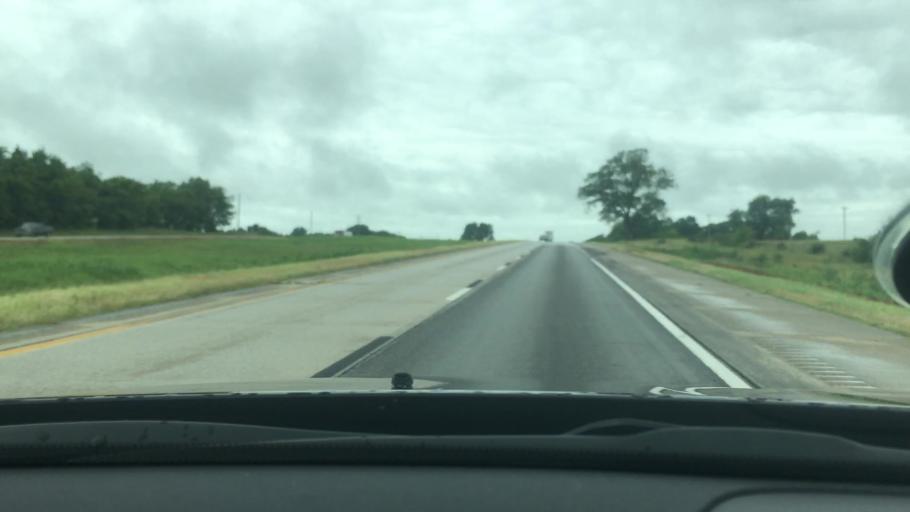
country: US
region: Oklahoma
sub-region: Bryan County
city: Durant
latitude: 34.1803
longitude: -96.2486
